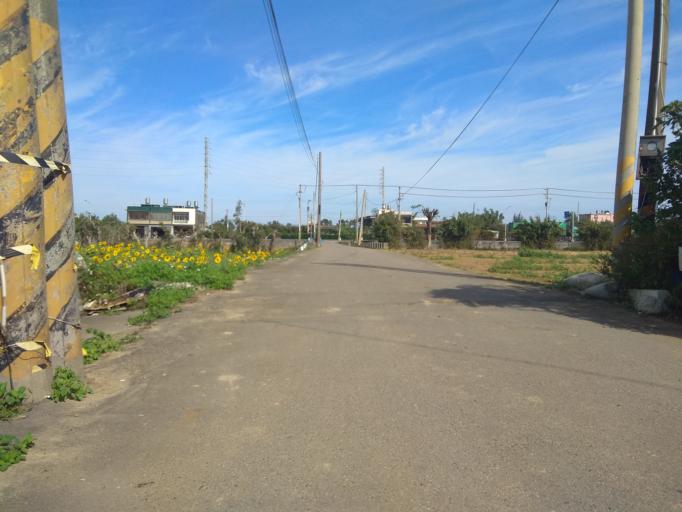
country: TW
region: Taiwan
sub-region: Hsinchu
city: Zhubei
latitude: 24.9869
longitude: 121.0386
